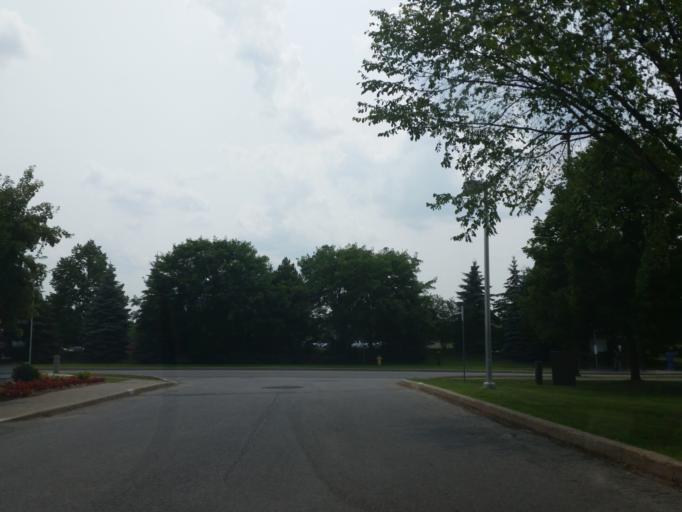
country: CA
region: Ontario
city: Bells Corners
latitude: 45.3437
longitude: -75.9127
